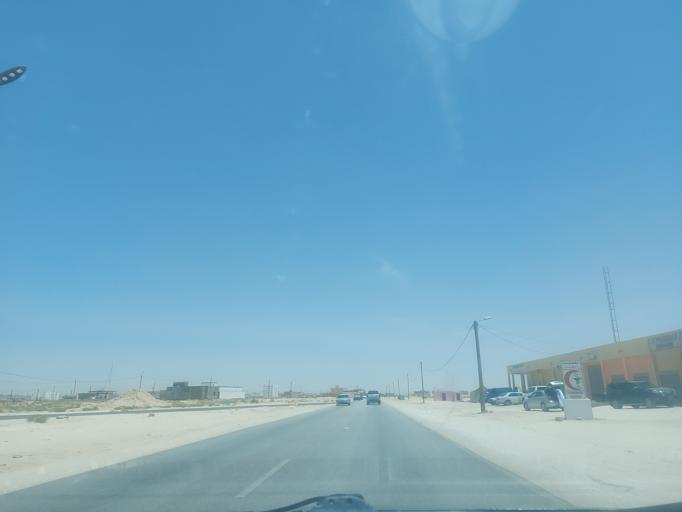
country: MR
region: Nouakchott
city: Nouakchott
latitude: 18.0784
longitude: -15.9550
